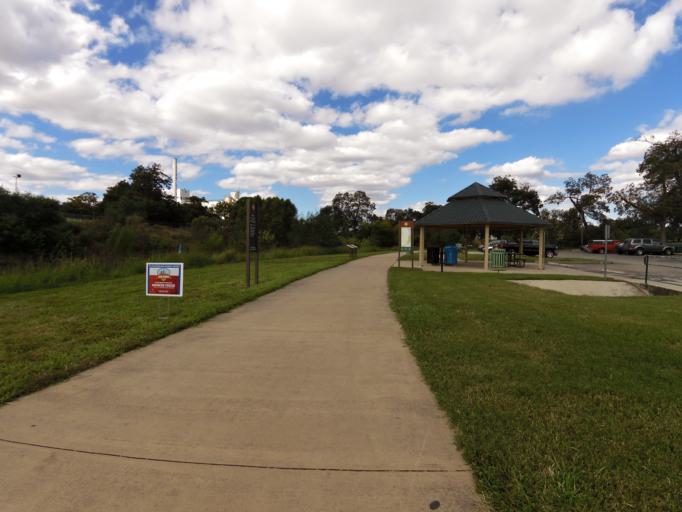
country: US
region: Texas
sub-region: Bexar County
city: San Antonio
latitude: 29.4002
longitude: -98.4889
